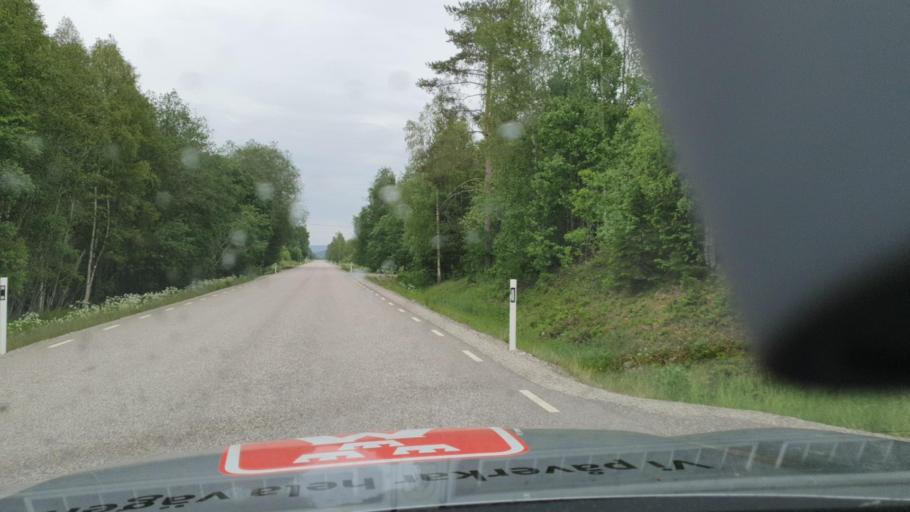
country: SE
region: Vaesternorrland
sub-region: Kramfors Kommun
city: Kramfors
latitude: 62.9189
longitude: 17.9546
